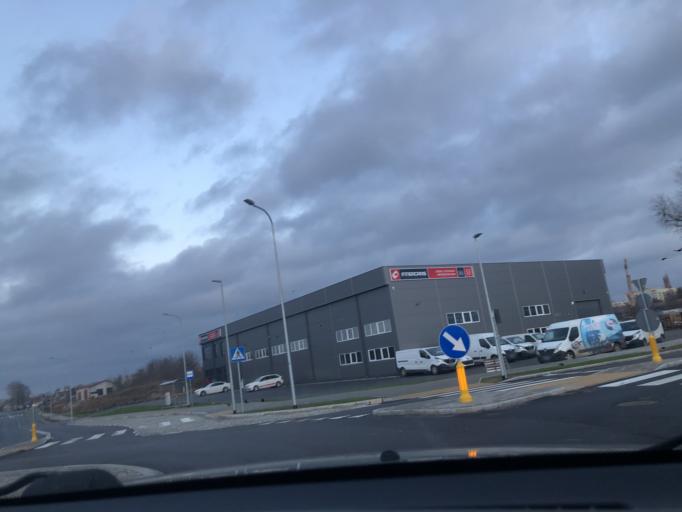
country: PL
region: Podlasie
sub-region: Lomza
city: Lomza
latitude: 53.1694
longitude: 22.0595
